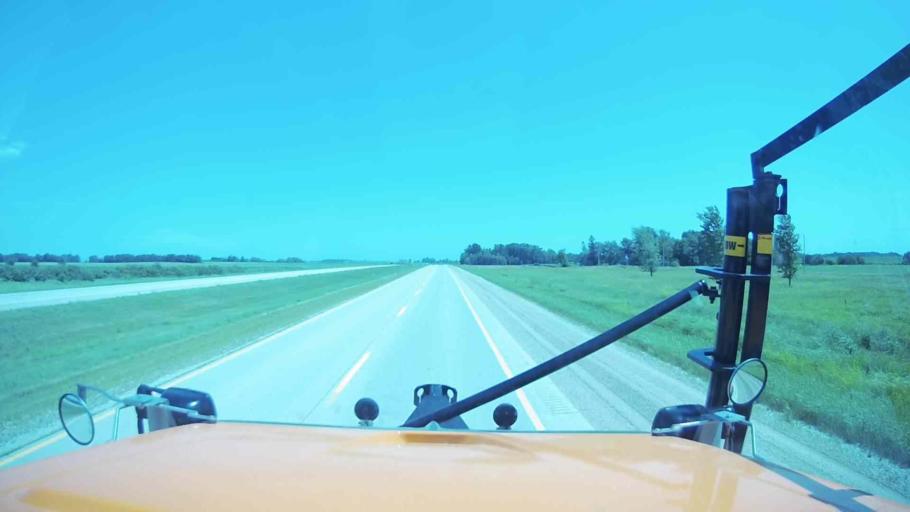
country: US
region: Iowa
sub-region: Floyd County
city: Nora Springs
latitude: 43.1162
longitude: -92.9778
